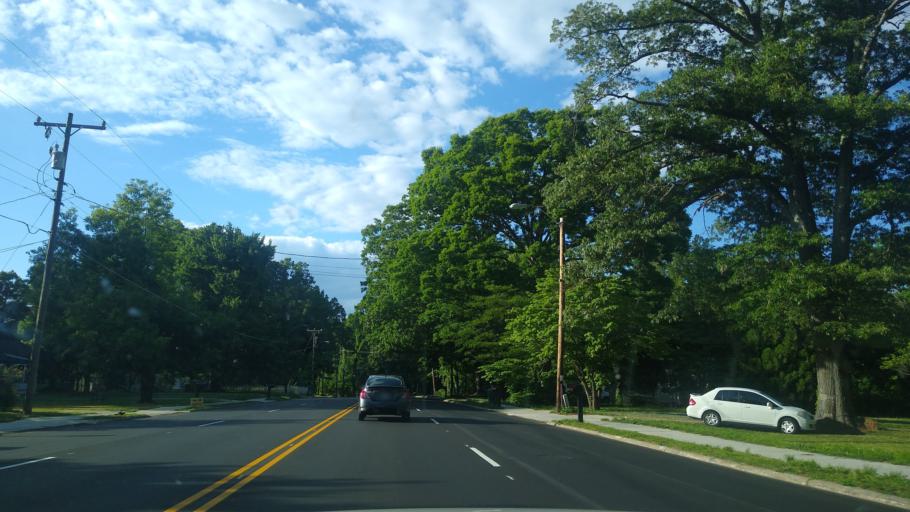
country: US
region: North Carolina
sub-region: Guilford County
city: Greensboro
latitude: 36.1238
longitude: -79.7728
